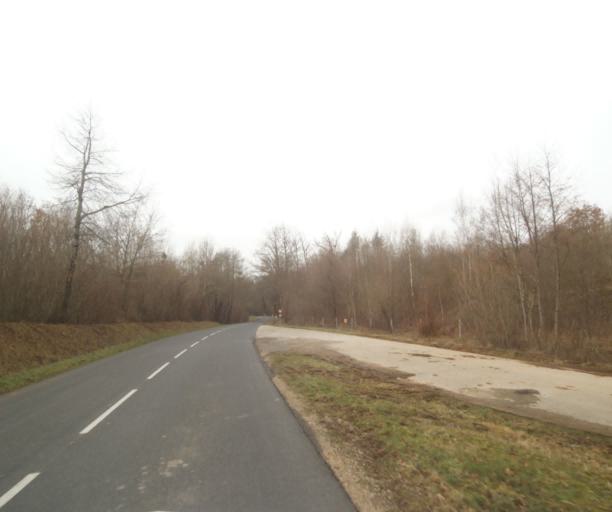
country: FR
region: Champagne-Ardenne
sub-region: Departement de la Marne
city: Pargny-sur-Saulx
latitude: 48.7379
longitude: 4.8776
